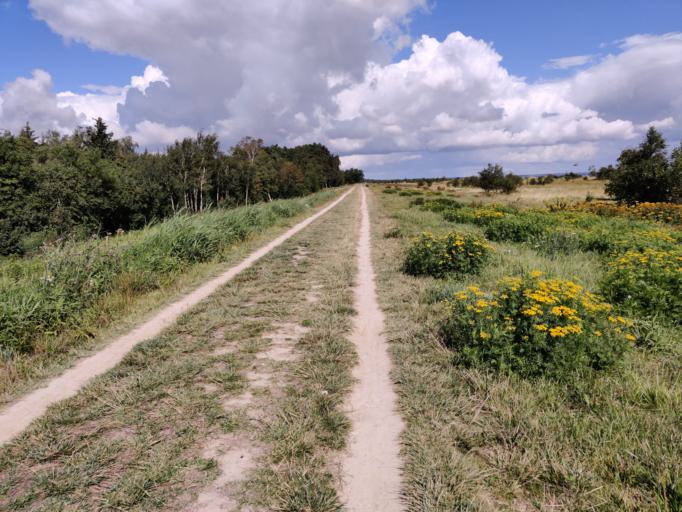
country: DK
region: Zealand
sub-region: Guldborgsund Kommune
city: Nykobing Falster
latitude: 54.6364
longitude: 11.9611
